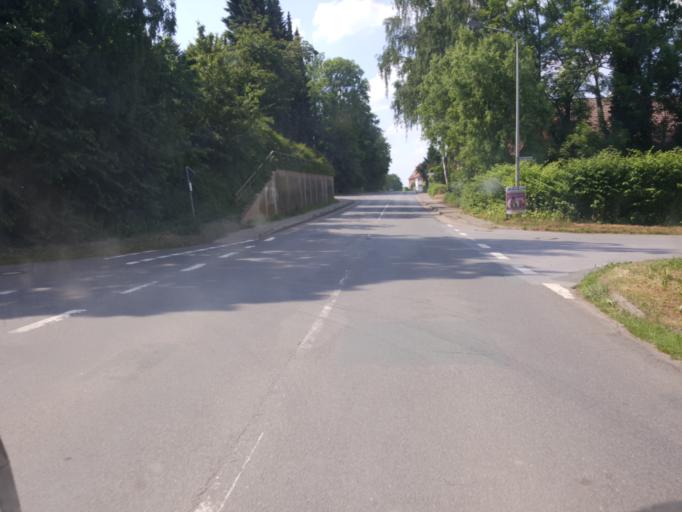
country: DE
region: North Rhine-Westphalia
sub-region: Regierungsbezirk Detmold
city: Hille
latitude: 52.2799
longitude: 8.7635
